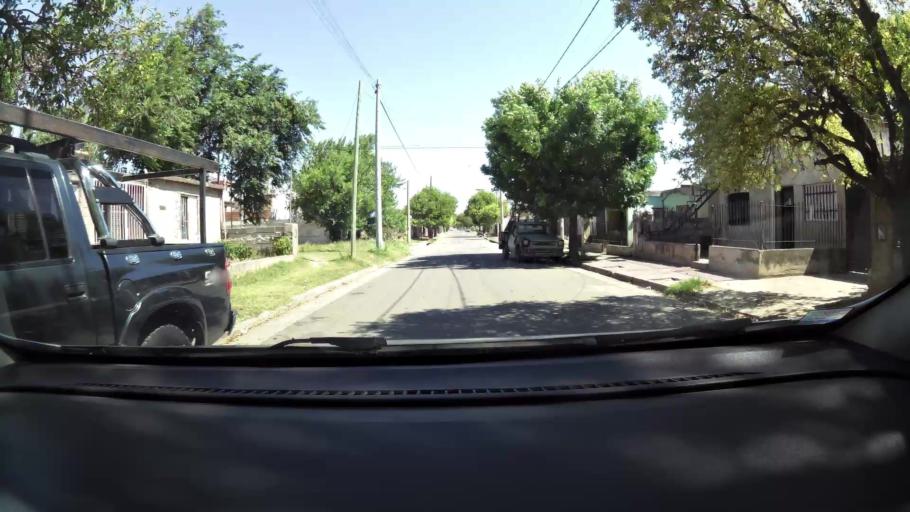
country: AR
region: Cordoba
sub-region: Departamento de Capital
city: Cordoba
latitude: -31.3687
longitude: -64.1365
